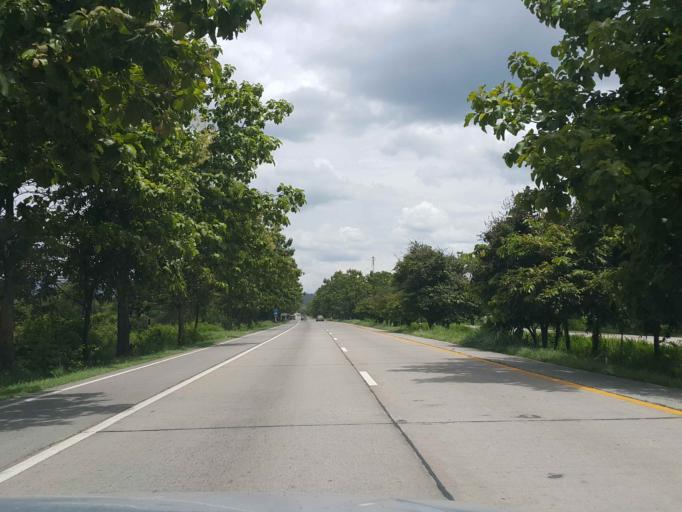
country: TH
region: Lamphun
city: Mae Tha
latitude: 18.5286
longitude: 99.0809
